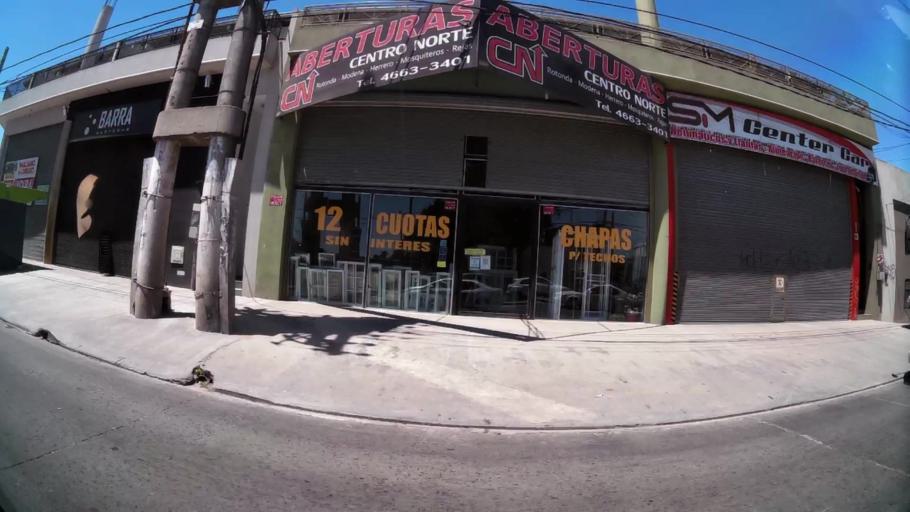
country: AR
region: Buenos Aires
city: Hurlingham
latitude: -34.4997
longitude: -58.7107
